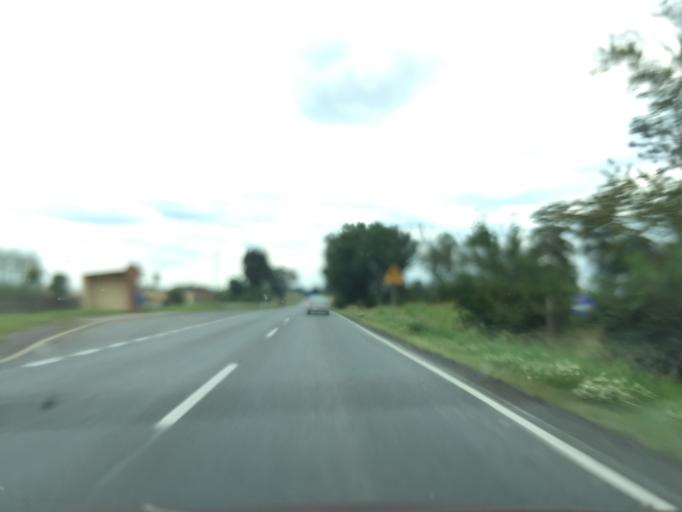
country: PL
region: Greater Poland Voivodeship
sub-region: Kalisz
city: Kalisz
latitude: 51.8265
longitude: 18.0943
